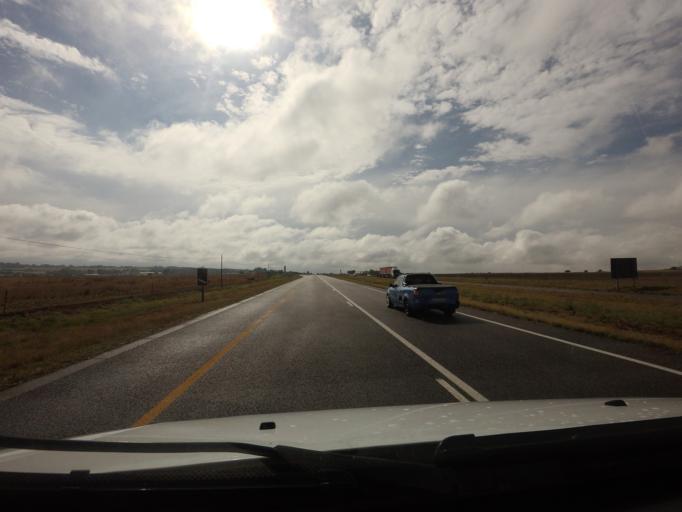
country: ZA
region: Gauteng
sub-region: City of Tshwane Metropolitan Municipality
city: Cullinan
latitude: -25.7981
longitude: 28.5625
